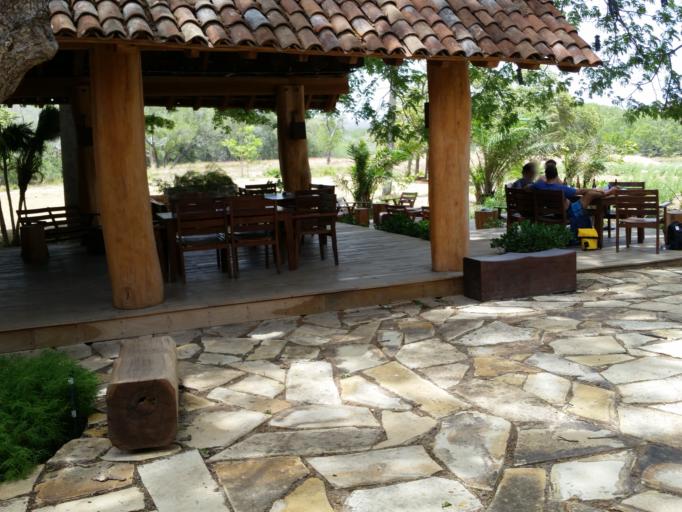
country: NI
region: Rivas
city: Tola
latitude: 11.4145
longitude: -86.0613
